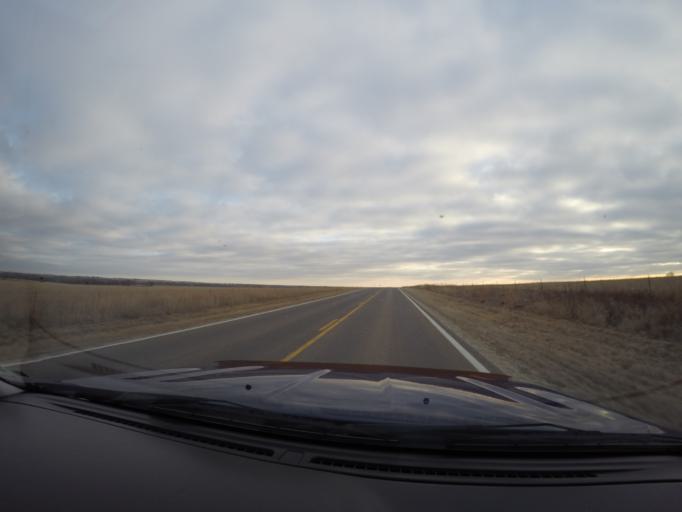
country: US
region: Kansas
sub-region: Morris County
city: Council Grove
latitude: 38.7579
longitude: -96.5012
